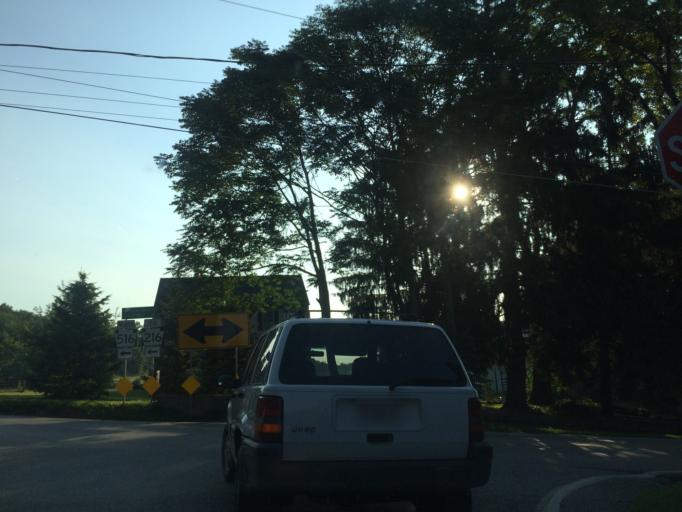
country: US
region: Pennsylvania
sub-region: York County
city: Glen Rock
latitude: 39.7477
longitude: -76.8044
